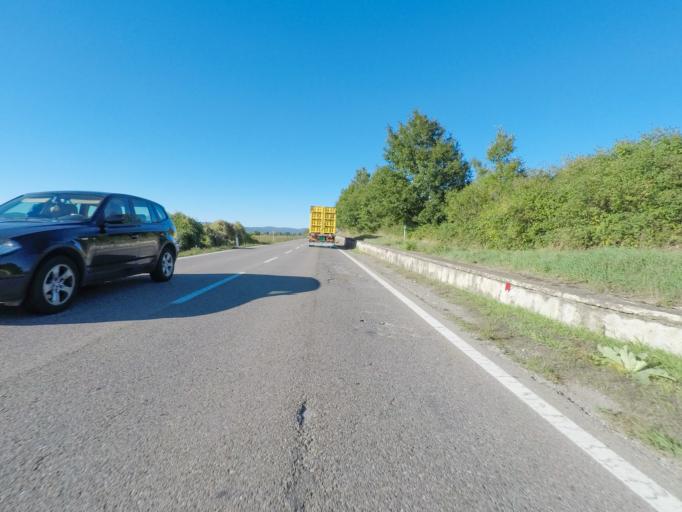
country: IT
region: Tuscany
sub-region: Provincia di Siena
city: Rosia
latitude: 43.2141
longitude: 11.2772
